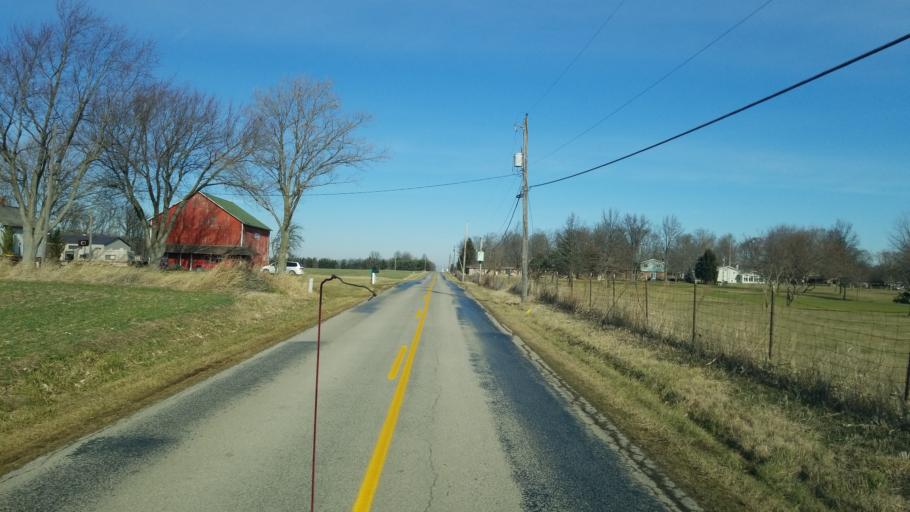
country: US
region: Ohio
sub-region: Allen County
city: Bluffton
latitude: 40.8656
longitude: -83.9379
